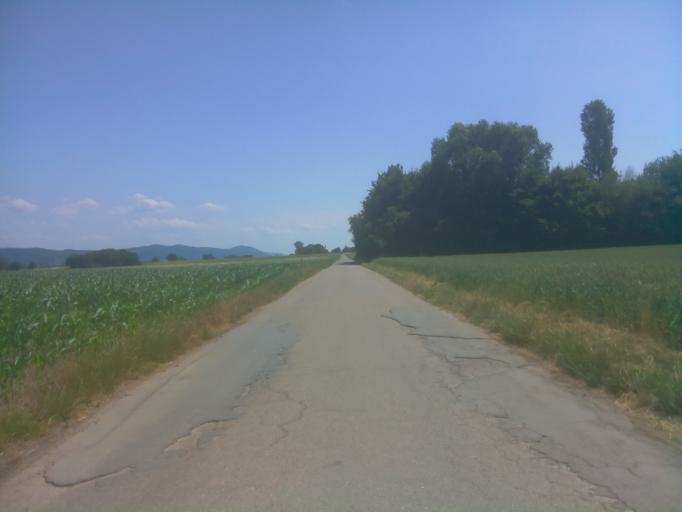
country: DE
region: Baden-Wuerttemberg
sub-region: Karlsruhe Region
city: Hemsbach
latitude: 49.5885
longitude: 8.6188
